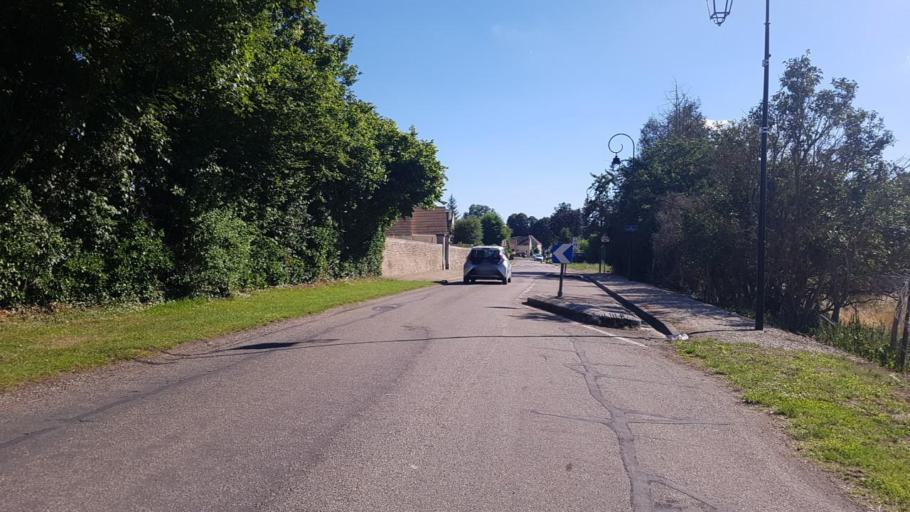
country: FR
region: Ile-de-France
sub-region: Departement de Seine-et-Marne
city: Coupvray
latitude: 48.9113
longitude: 2.7830
